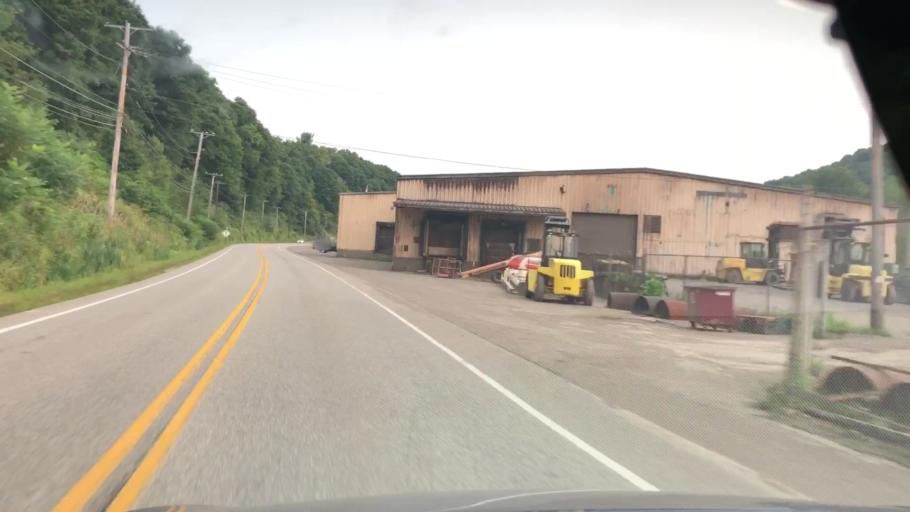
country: US
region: Pennsylvania
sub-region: Venango County
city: Hasson Heights
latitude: 41.4655
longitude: -79.6904
